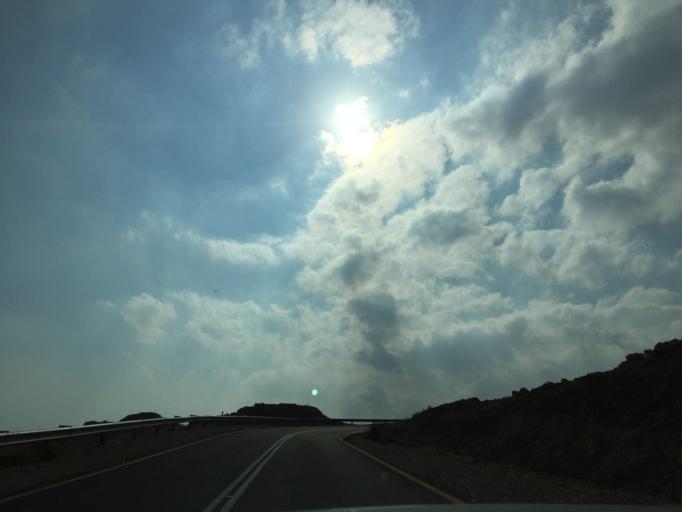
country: IL
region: Southern District
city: `En Boqeq
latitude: 31.3188
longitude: 35.3321
